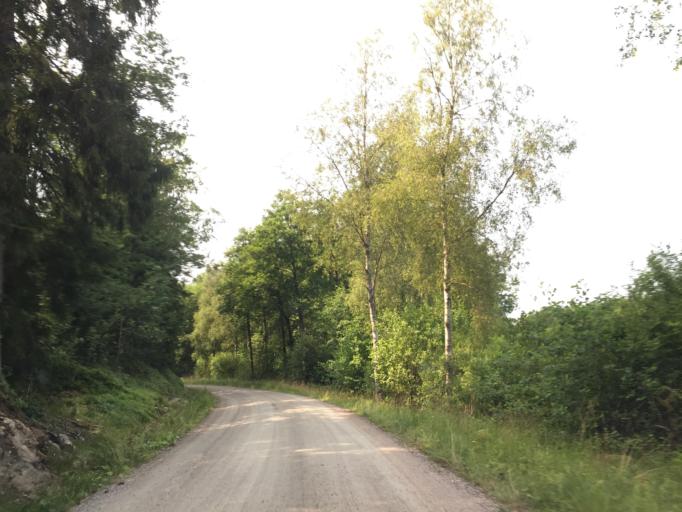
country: SE
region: Vaestra Goetaland
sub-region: Lilla Edets Kommun
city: Lilla Edet
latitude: 58.2372
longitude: 12.1036
